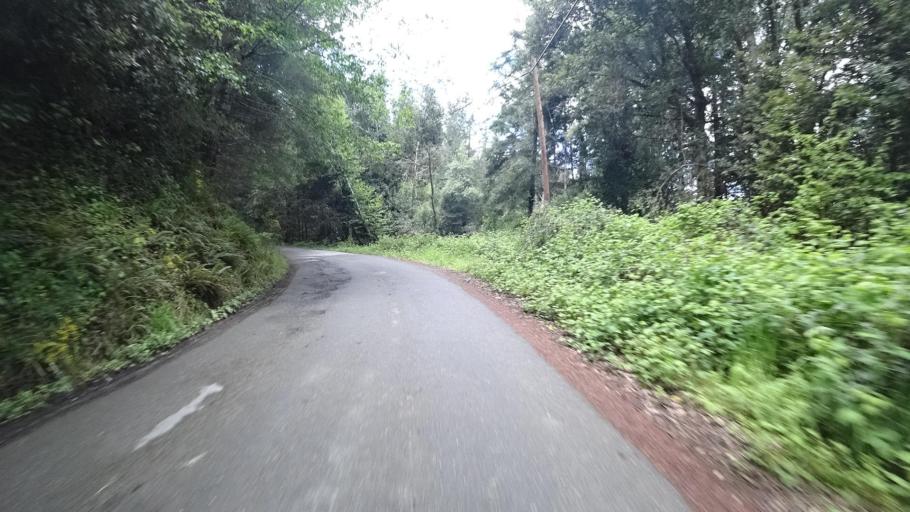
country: US
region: California
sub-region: Humboldt County
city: Blue Lake
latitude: 40.7650
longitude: -123.8792
